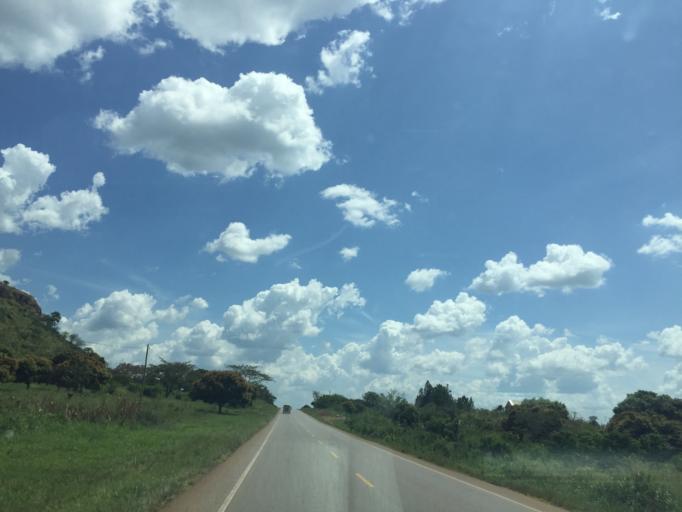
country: UG
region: Central Region
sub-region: Nakasongola District
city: Nakasongola
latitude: 1.3142
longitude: 32.4221
